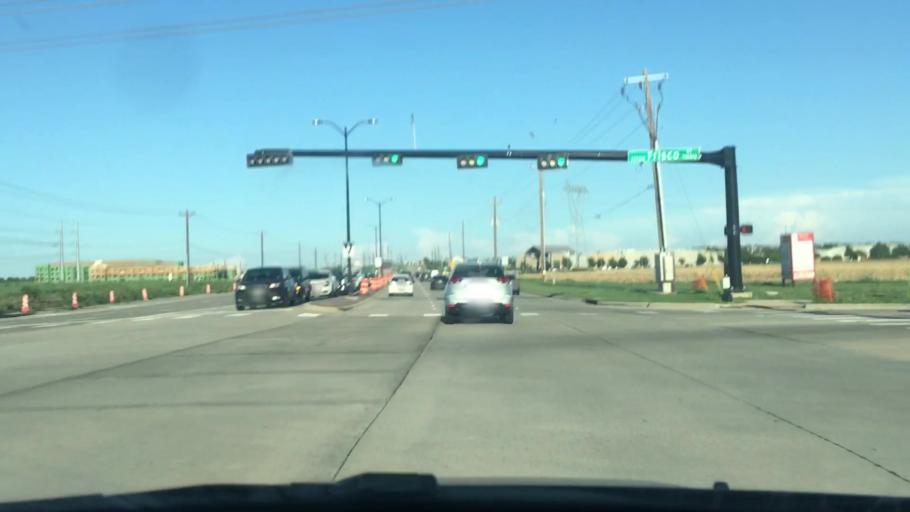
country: US
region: Texas
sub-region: Collin County
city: Frisco
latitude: 33.1746
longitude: -96.8323
